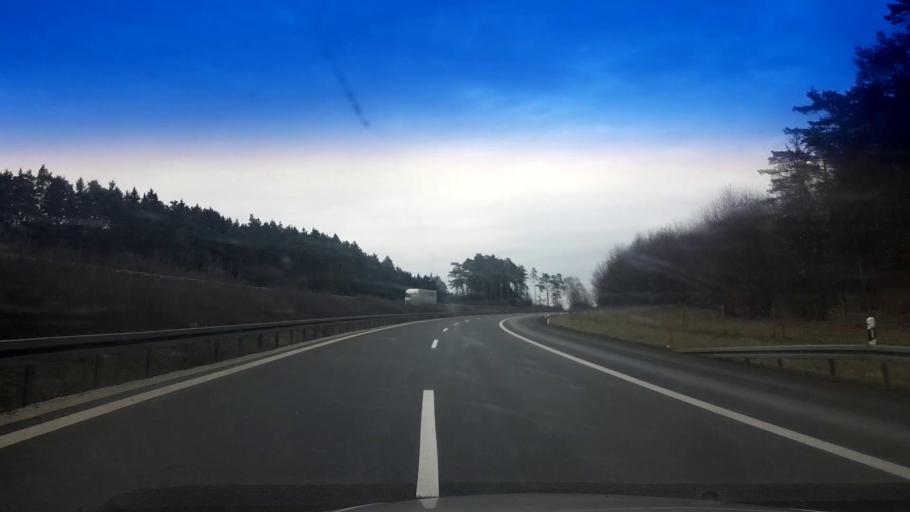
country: DE
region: Bavaria
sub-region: Upper Franconia
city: Wattendorf
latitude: 49.9876
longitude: 11.0985
